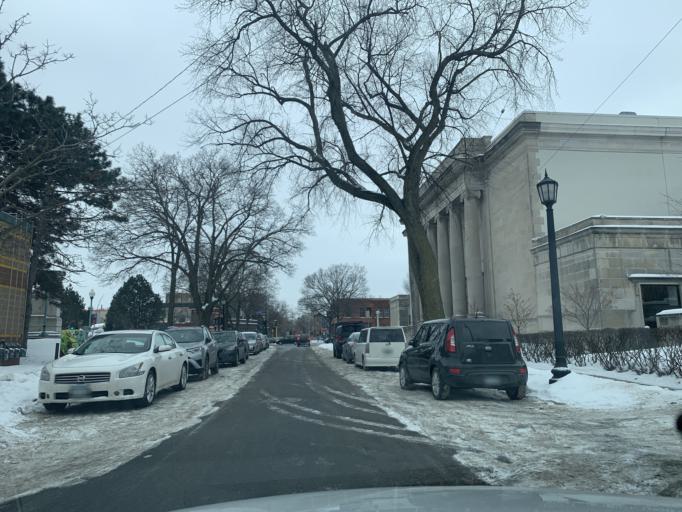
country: US
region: Minnesota
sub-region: Hennepin County
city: Minneapolis
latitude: 44.9599
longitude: -93.2944
